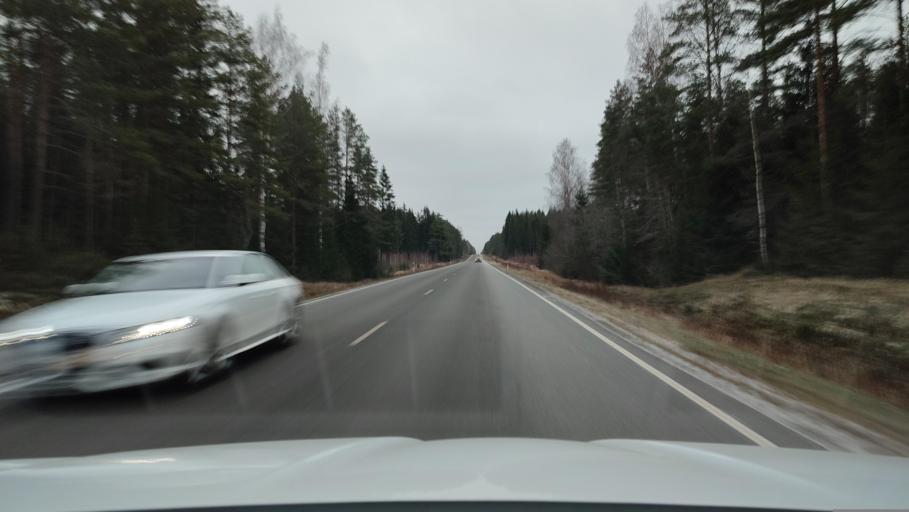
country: FI
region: Ostrobothnia
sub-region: Sydosterbotten
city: Naerpes
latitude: 62.5553
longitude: 21.4758
